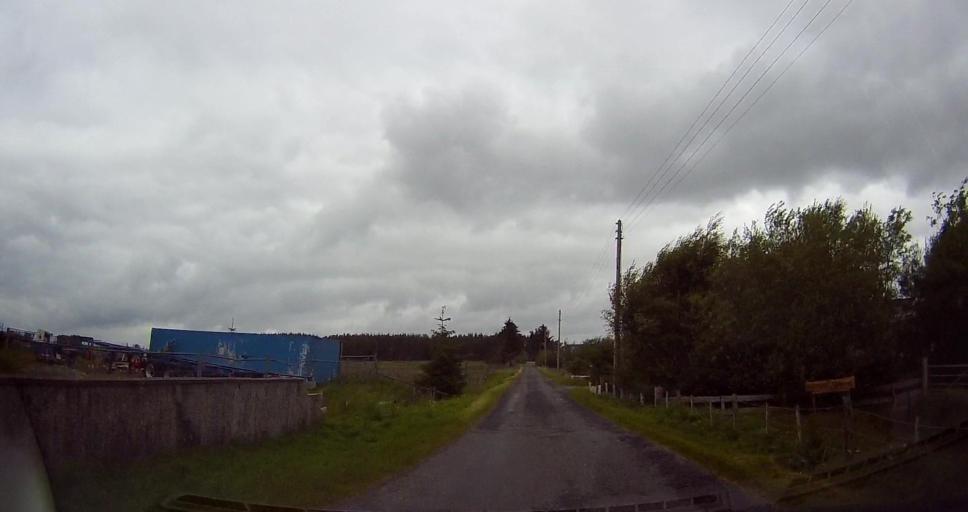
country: GB
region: Scotland
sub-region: Highland
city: Alness
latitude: 58.0636
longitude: -4.4274
